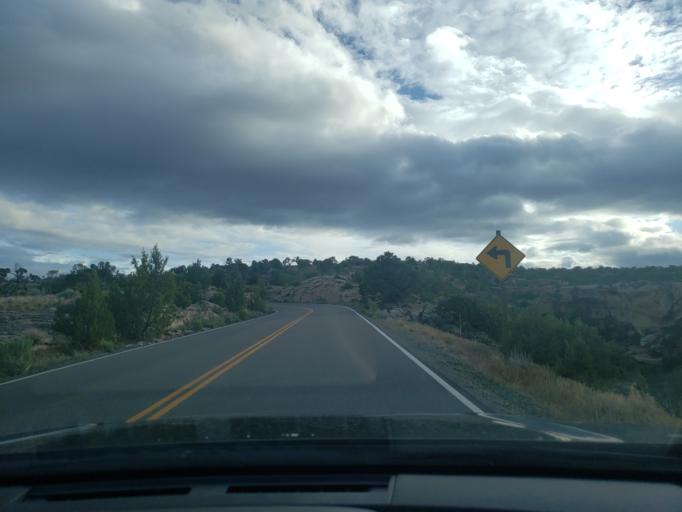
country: US
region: Colorado
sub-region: Mesa County
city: Redlands
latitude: 39.0349
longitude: -108.6466
